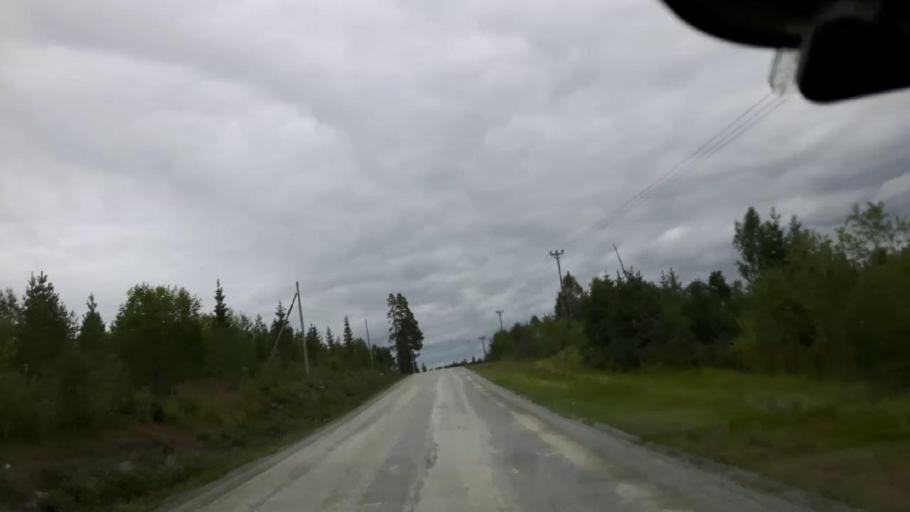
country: SE
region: Jaemtland
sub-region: OEstersunds Kommun
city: Brunflo
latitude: 63.0954
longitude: 15.1325
